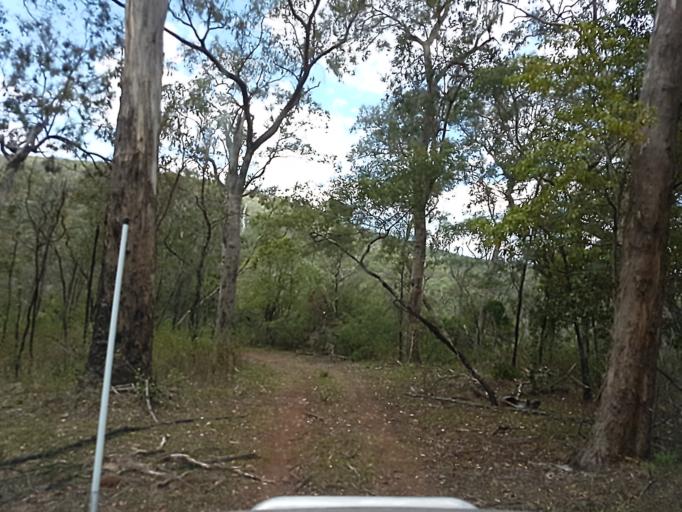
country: AU
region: Victoria
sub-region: East Gippsland
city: Lakes Entrance
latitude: -37.3634
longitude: 148.3538
